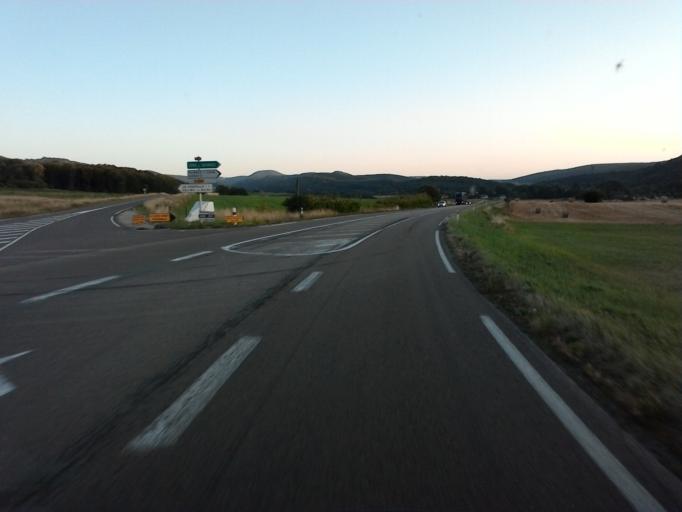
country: FR
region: Franche-Comte
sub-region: Departement du Jura
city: Salins-les-Bains
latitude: 47.0214
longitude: 5.8674
